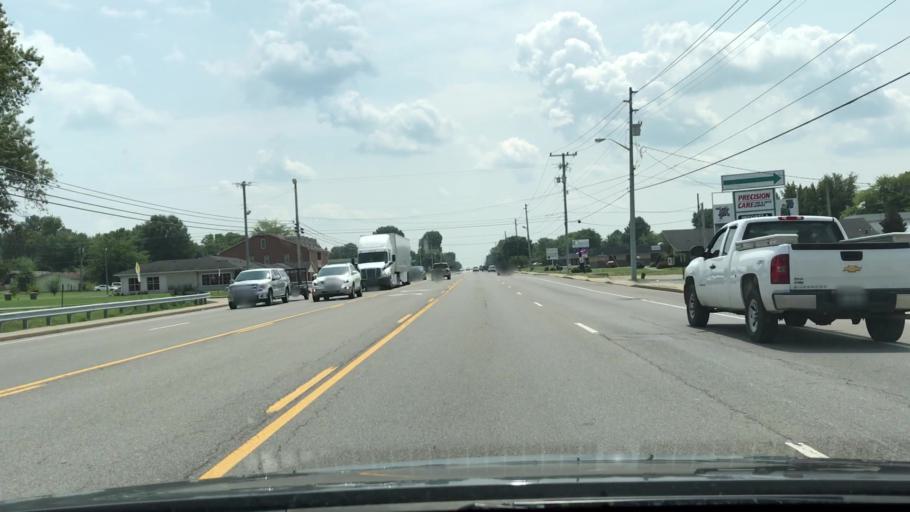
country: US
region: Tennessee
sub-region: Sumner County
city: Portland
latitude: 36.5705
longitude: -86.5125
